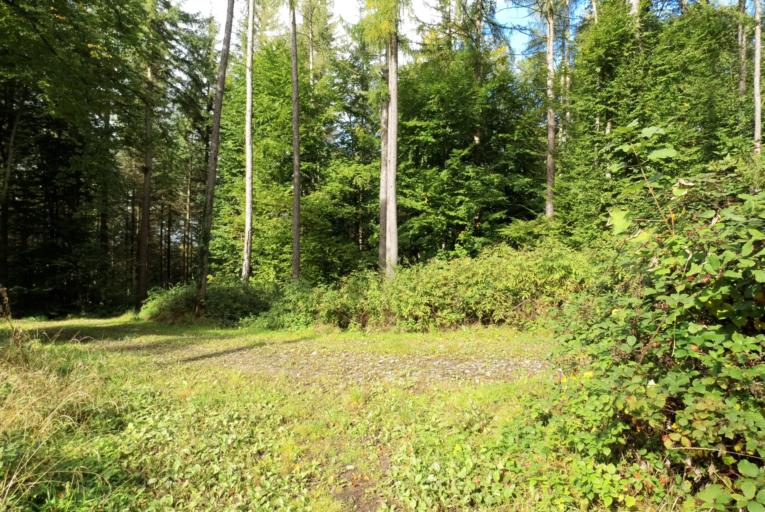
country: DE
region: Baden-Wuerttemberg
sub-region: Karlsruhe Region
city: Aglasterhausen
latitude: 49.3424
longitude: 8.9824
